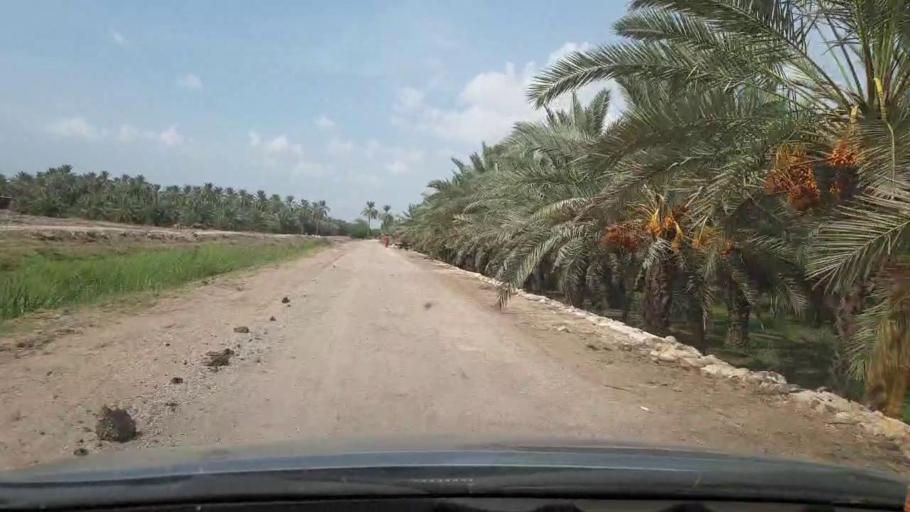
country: PK
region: Sindh
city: Khairpur
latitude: 27.5195
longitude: 68.8829
